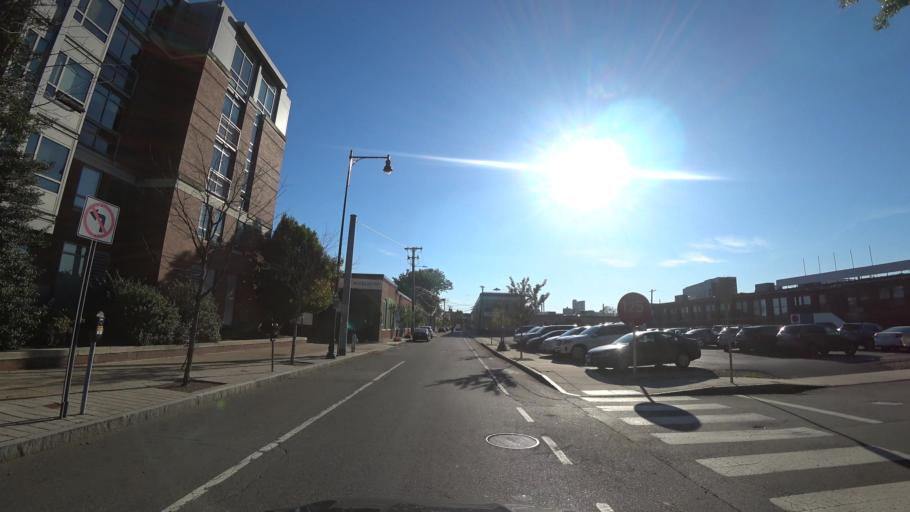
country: US
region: Massachusetts
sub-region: Middlesex County
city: Cambridge
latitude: 42.3600
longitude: -71.1029
